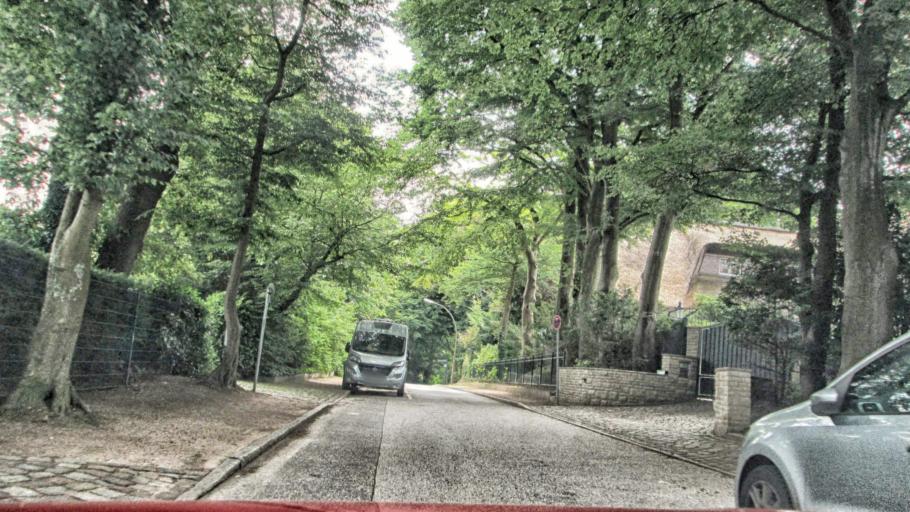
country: DE
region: Schleswig-Holstein
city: Halstenbek
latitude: 53.5639
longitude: 9.7985
